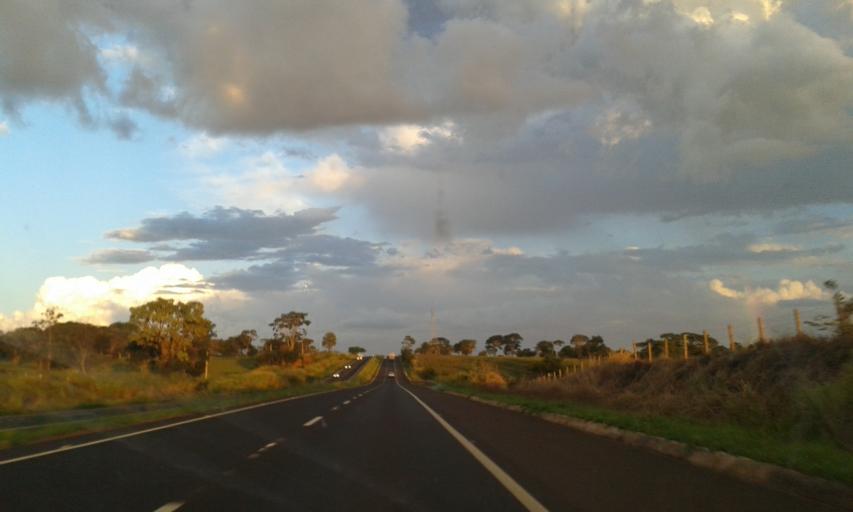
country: BR
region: Minas Gerais
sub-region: Monte Alegre De Minas
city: Monte Alegre de Minas
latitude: -18.8760
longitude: -48.7481
